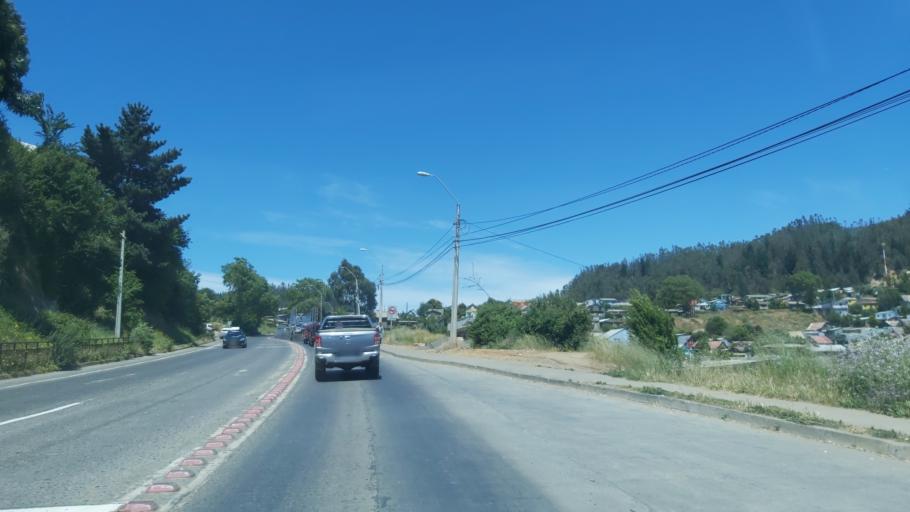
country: CL
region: Maule
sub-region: Provincia de Talca
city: Constitucion
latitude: -35.3411
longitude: -72.4194
